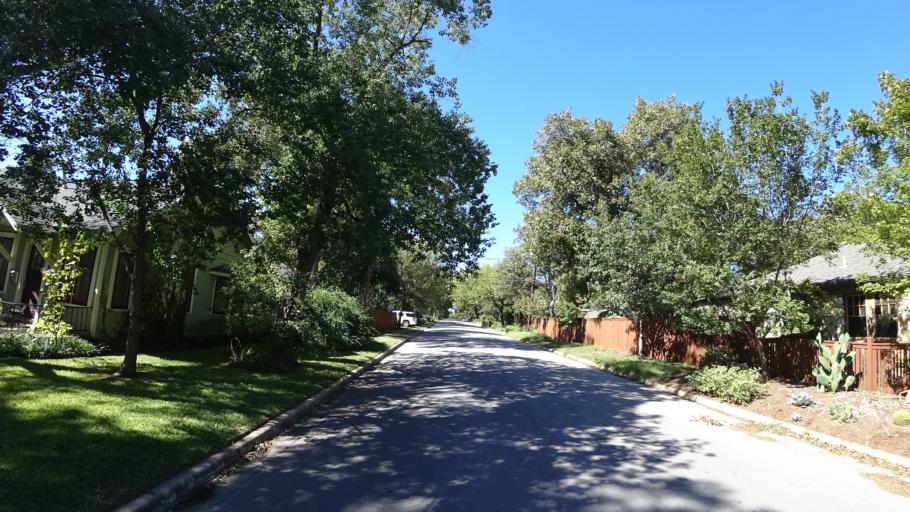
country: US
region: Texas
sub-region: Travis County
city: Austin
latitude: 30.3112
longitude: -97.7456
